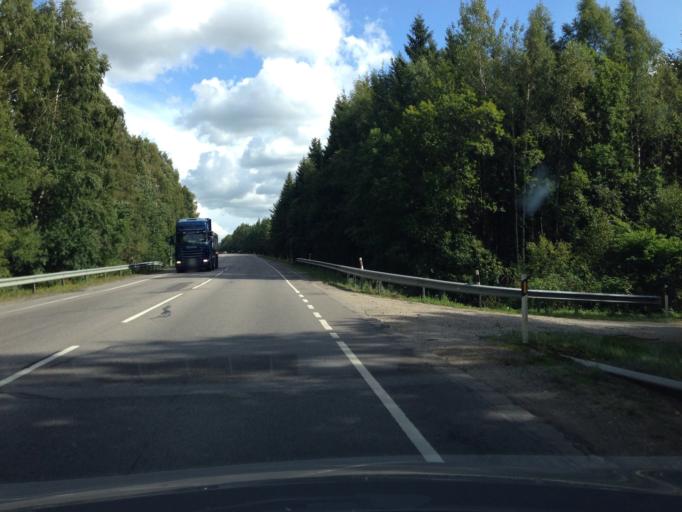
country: EE
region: Harju
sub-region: Saku vald
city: Saku
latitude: 59.3122
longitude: 24.6977
